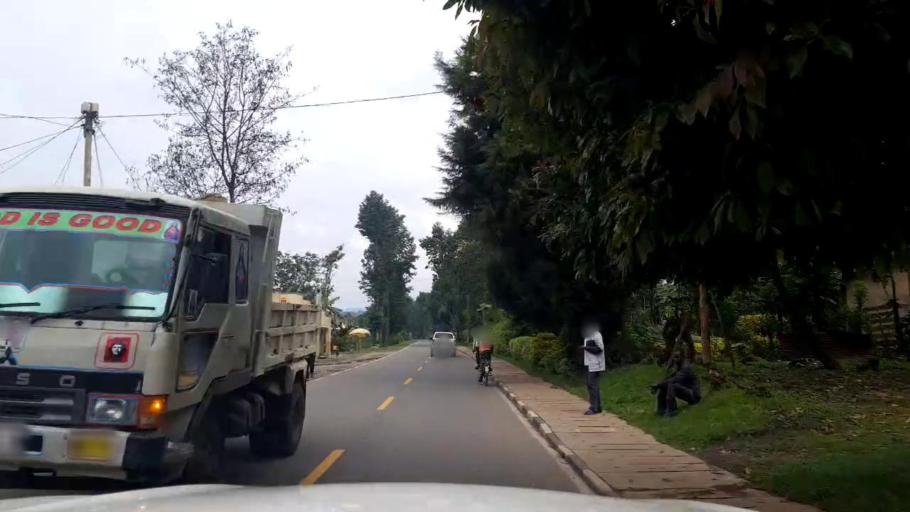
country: RW
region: Northern Province
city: Musanze
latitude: -1.4598
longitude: 29.6126
